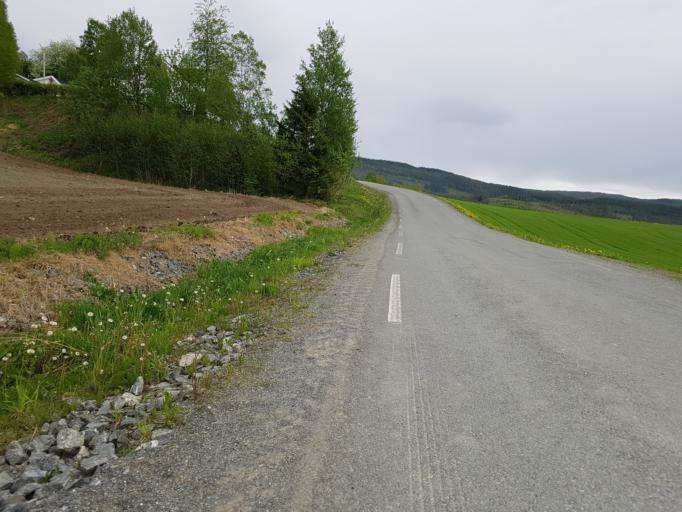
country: NO
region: Nord-Trondelag
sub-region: Levanger
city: Skogn
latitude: 63.6247
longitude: 11.2754
